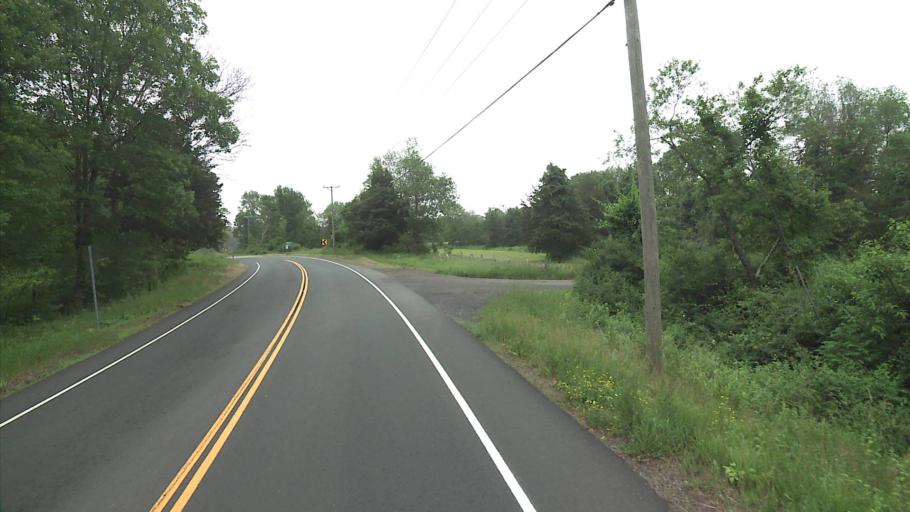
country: US
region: Connecticut
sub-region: Hartford County
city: Terramuggus
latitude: 41.6926
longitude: -72.4537
